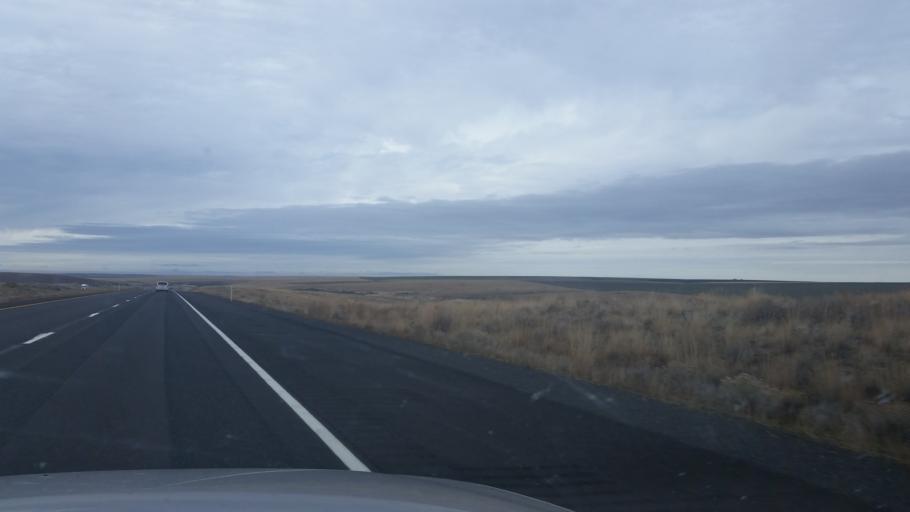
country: US
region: Washington
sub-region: Adams County
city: Ritzville
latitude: 47.1108
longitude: -118.5316
